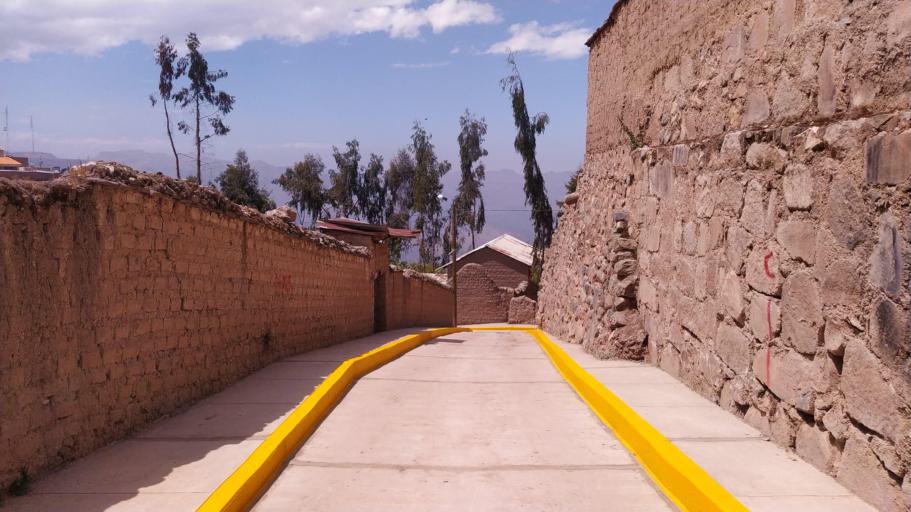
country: PE
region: Lima
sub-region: Provincia de Huarochiri
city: Cocachacra
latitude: -12.0004
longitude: -76.4760
